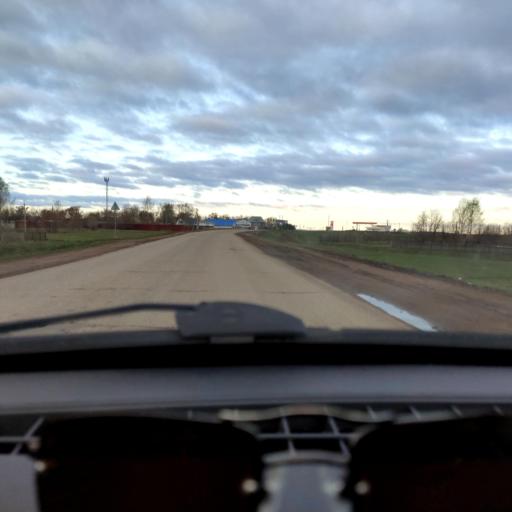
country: RU
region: Bashkortostan
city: Kabakovo
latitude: 54.5485
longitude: 56.0924
